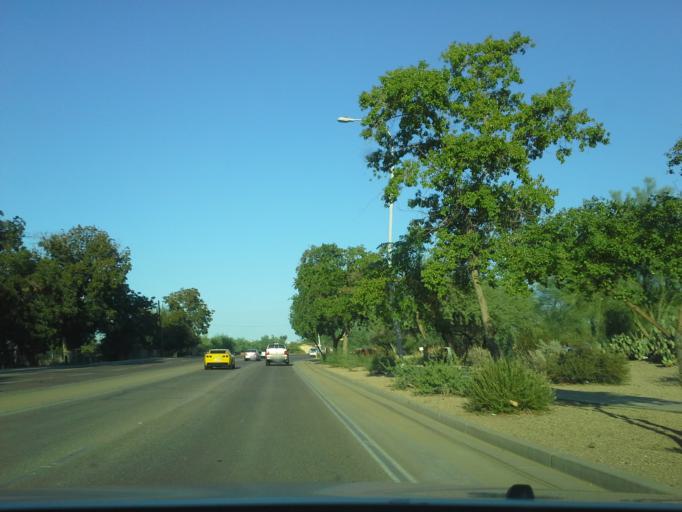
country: US
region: Arizona
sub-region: Maricopa County
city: Guadalupe
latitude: 33.3937
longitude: -112.0183
